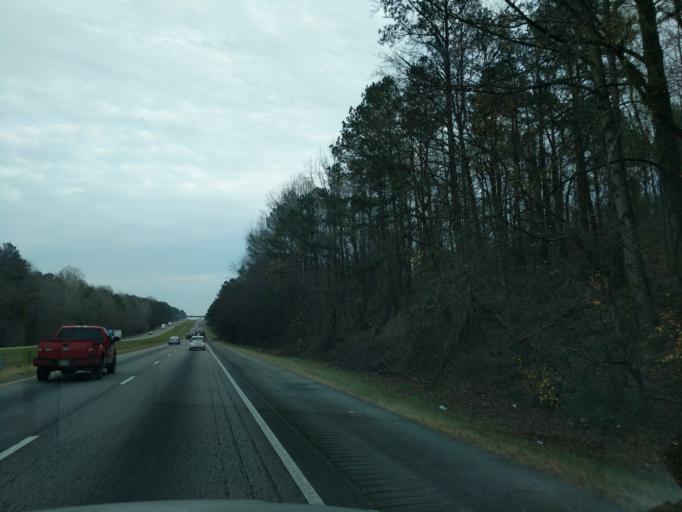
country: US
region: Georgia
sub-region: Jackson County
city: Braselton
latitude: 34.1267
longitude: -83.7320
